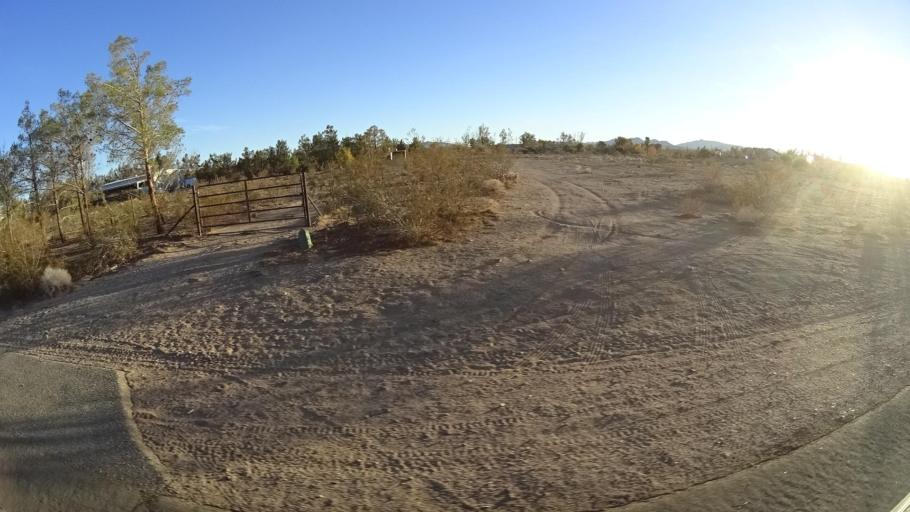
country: US
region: California
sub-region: Kern County
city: Ridgecrest
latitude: 35.6301
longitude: -117.7168
